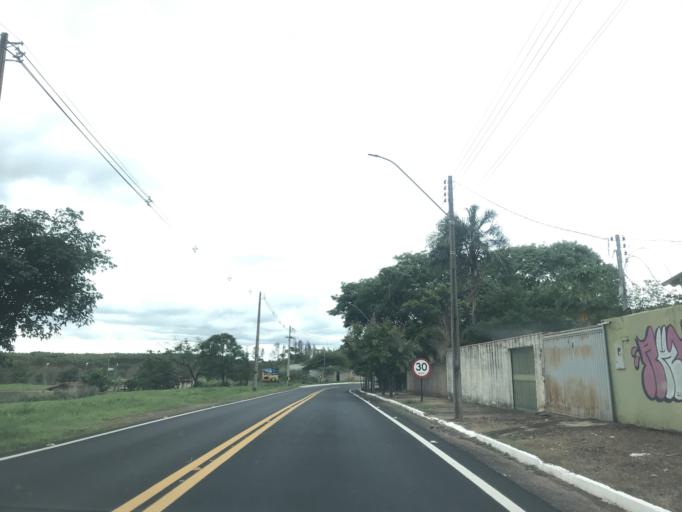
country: BR
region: Goias
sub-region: Caldas Novas
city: Caldas Novas
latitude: -17.7668
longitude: -48.7589
